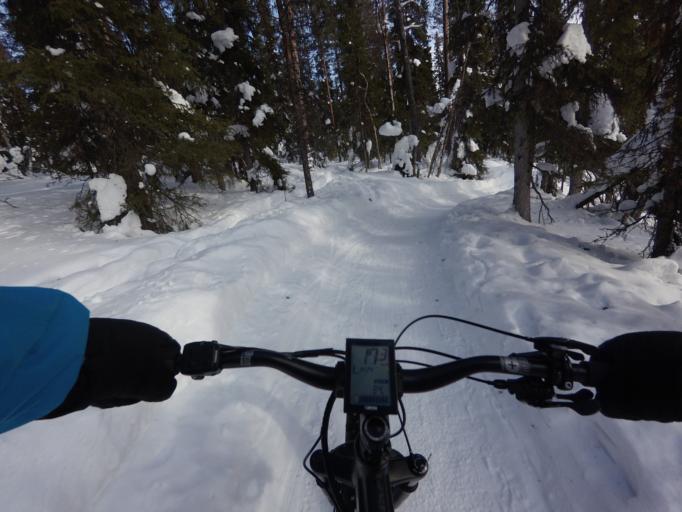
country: FI
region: Lapland
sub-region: Tunturi-Lappi
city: Kolari
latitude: 67.6020
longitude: 24.2319
